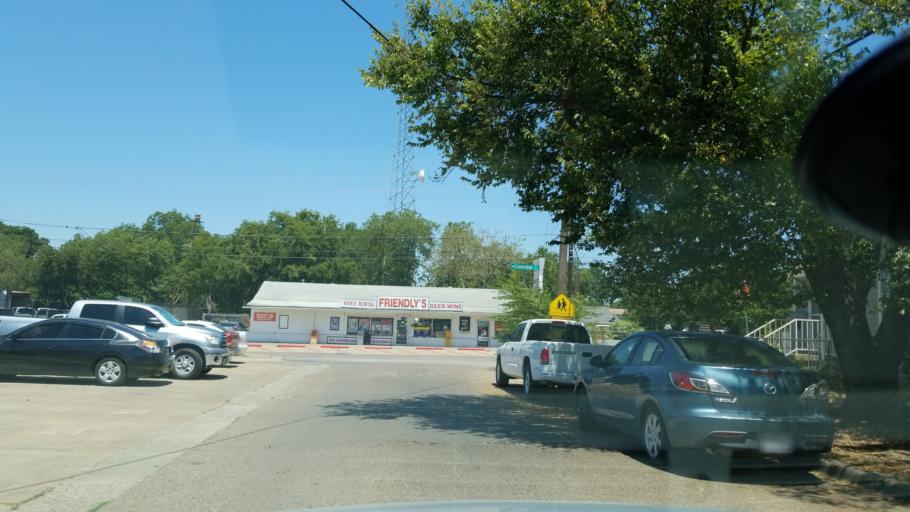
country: US
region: Texas
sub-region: Dallas County
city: Cockrell Hill
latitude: 32.7346
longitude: -96.8877
